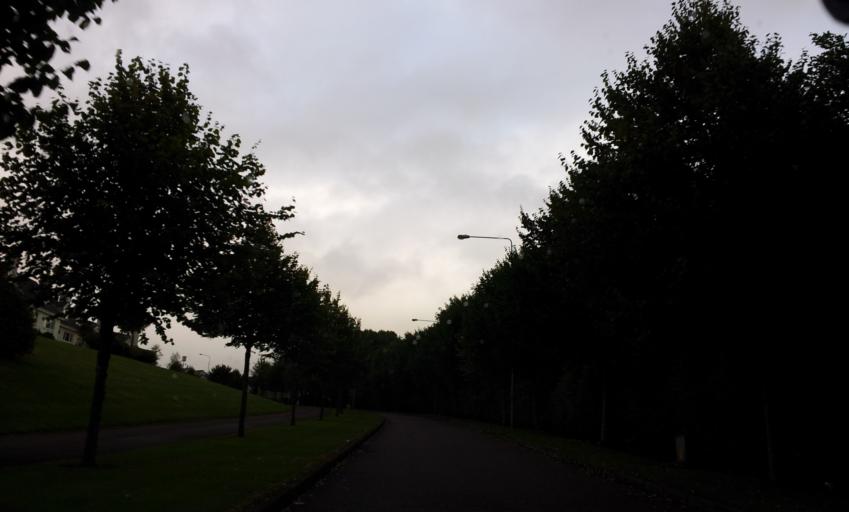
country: IE
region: Munster
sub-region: County Cork
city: Carrigaline
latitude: 51.8685
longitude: -8.4111
